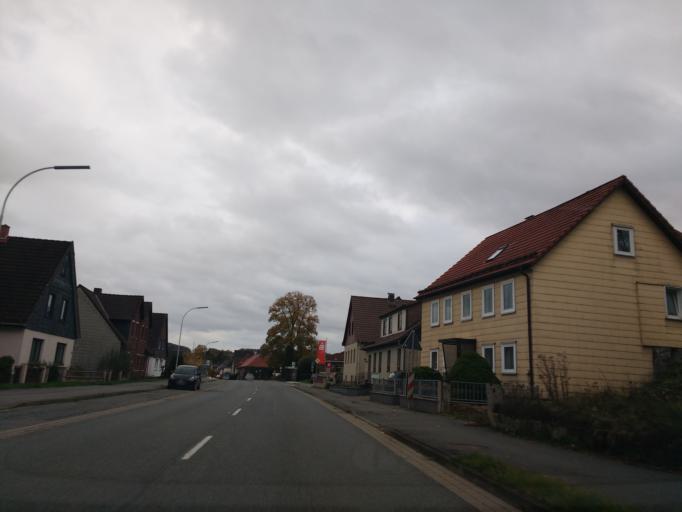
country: DE
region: Lower Saxony
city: Bad Lauterberg im Harz
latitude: 51.6170
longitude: 10.4161
